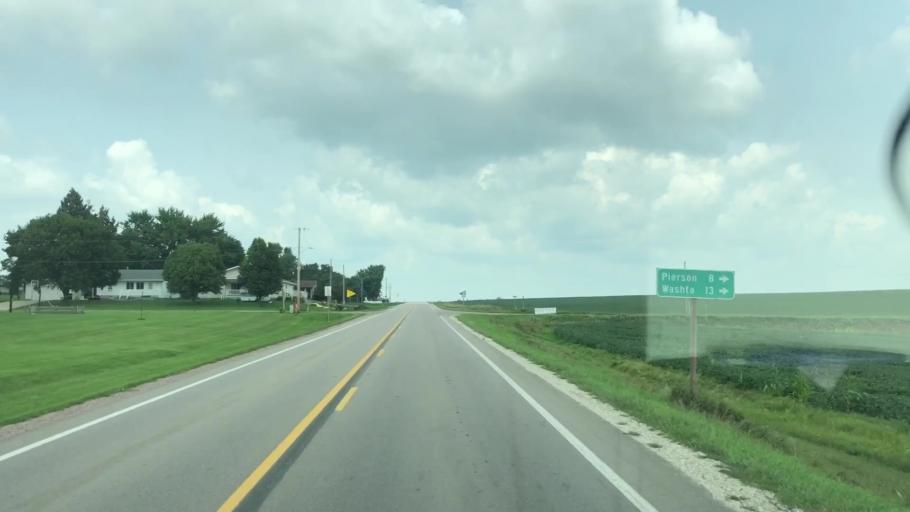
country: US
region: Iowa
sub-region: Plymouth County
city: Kingsley
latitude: 42.5890
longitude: -95.9574
